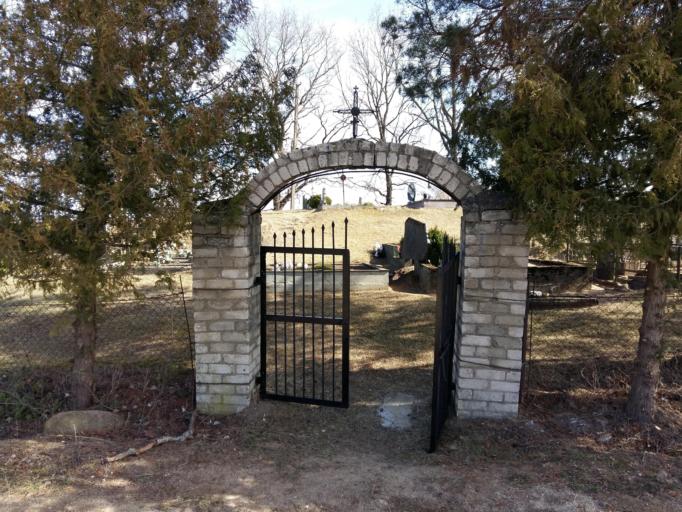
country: LT
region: Alytaus apskritis
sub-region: Alytaus rajonas
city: Daugai
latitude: 54.2353
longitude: 24.2249
